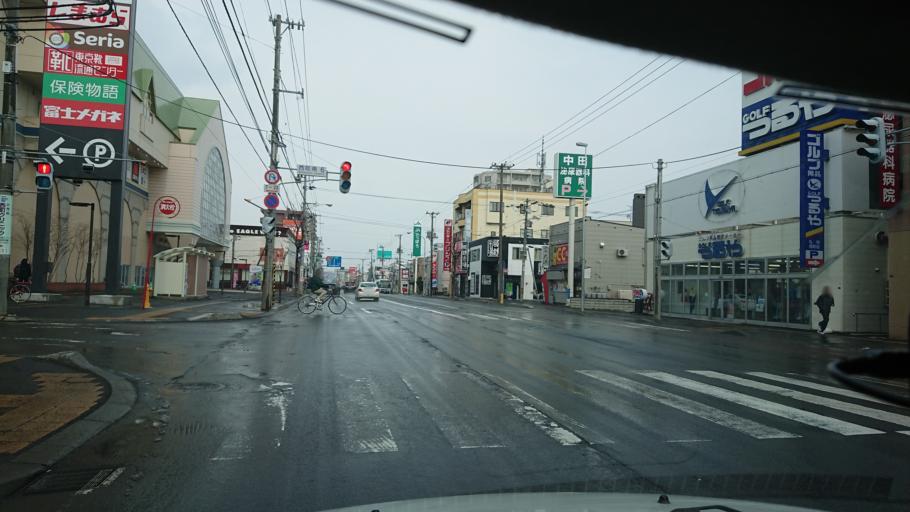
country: JP
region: Hokkaido
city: Sapporo
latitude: 43.0783
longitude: 141.2900
